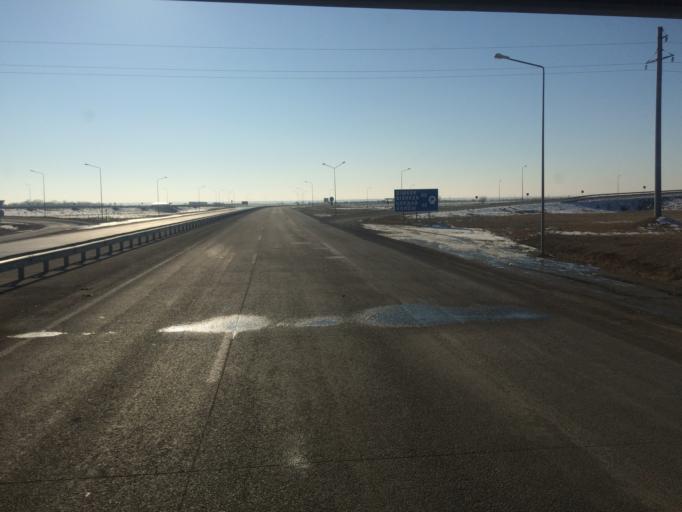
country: KG
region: Chuy
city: Sokuluk
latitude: 43.2756
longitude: 74.2307
